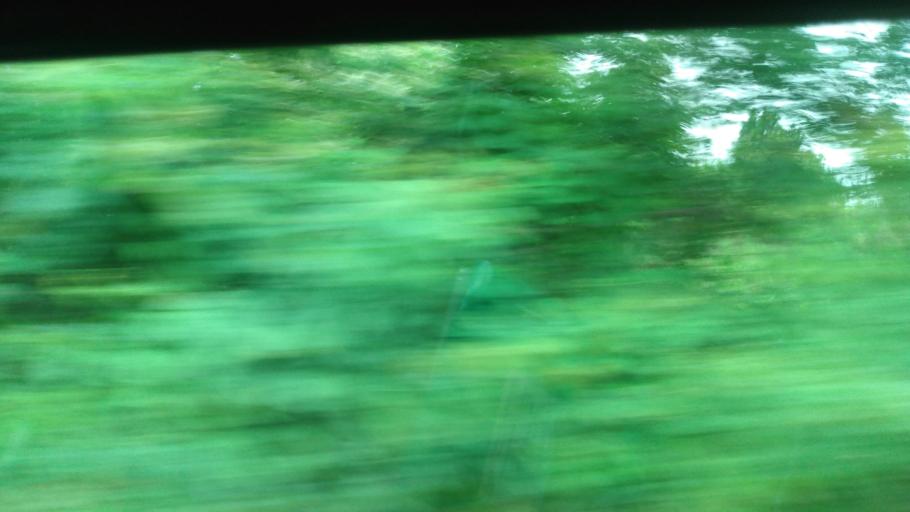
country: BR
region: Pernambuco
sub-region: Quipapa
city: Quipapa
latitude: -8.8005
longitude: -36.0003
